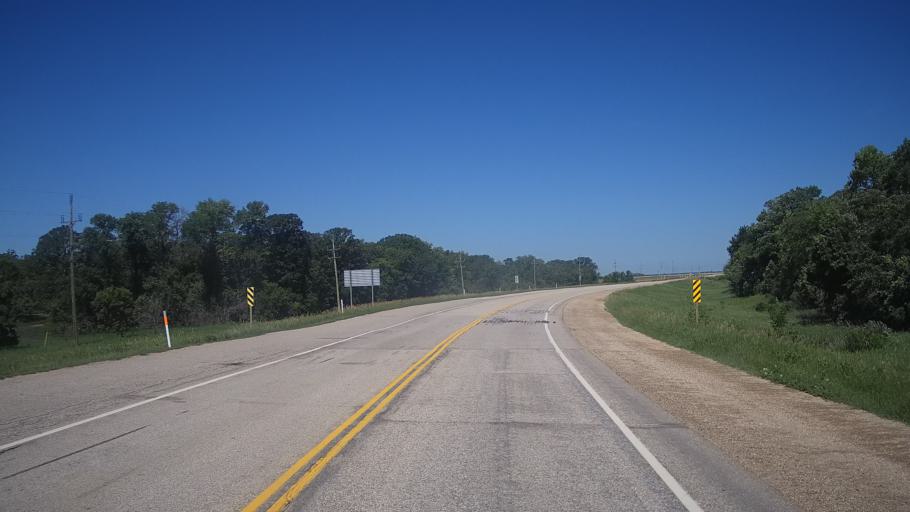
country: CA
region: Manitoba
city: Portage la Prairie
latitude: 50.1305
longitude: -98.5881
